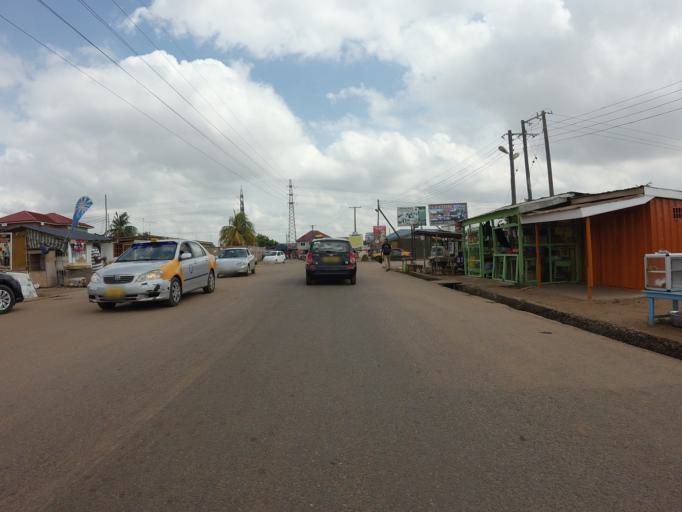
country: GH
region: Greater Accra
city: Nungua
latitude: 5.6186
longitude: -0.0927
